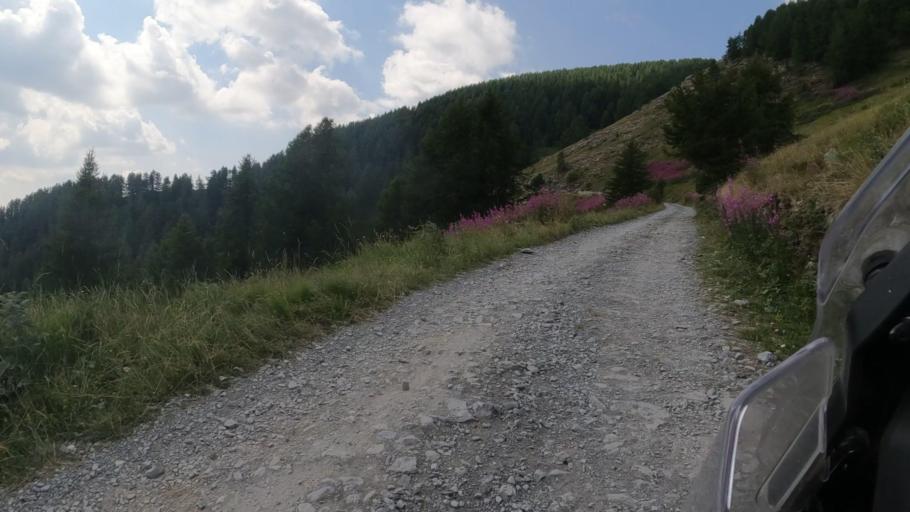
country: IT
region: Liguria
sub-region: Provincia di Imperia
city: Pigna
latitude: 44.0249
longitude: 7.6637
